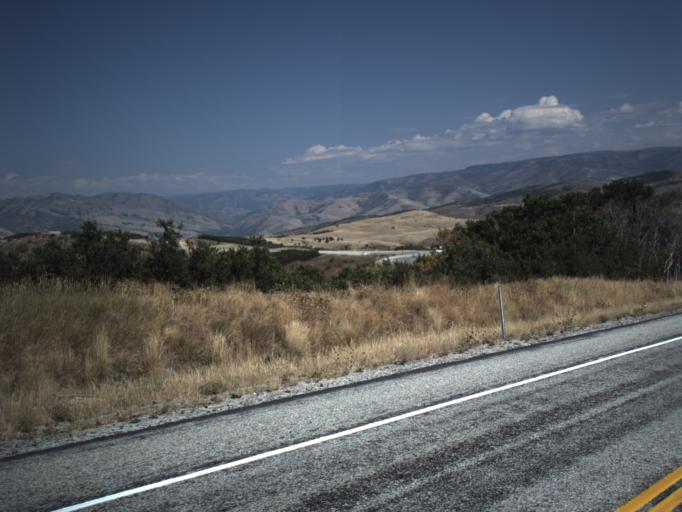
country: US
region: Utah
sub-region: Morgan County
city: Mountain Green
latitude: 41.2055
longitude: -111.8223
